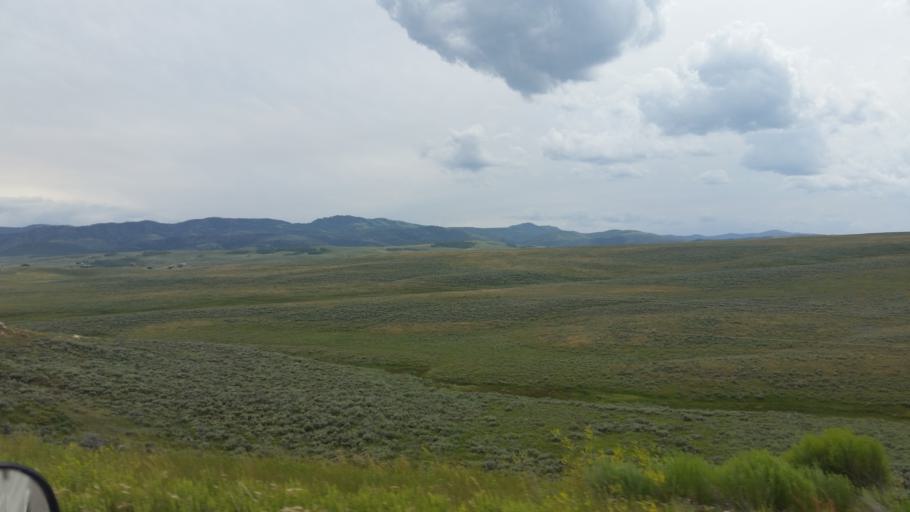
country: US
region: Utah
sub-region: Wasatch County
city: Heber
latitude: 40.1860
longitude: -111.0630
